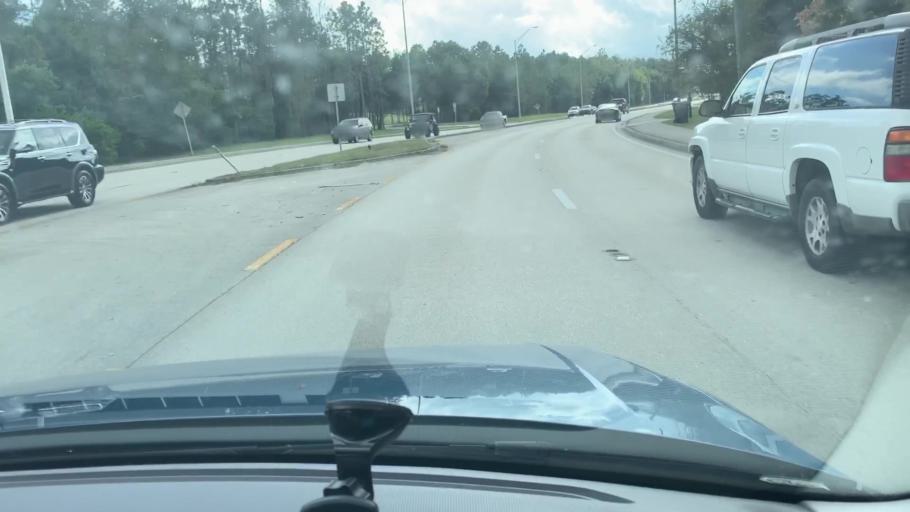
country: US
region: Florida
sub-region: Polk County
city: Gibsonia
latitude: 28.0953
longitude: -81.9986
